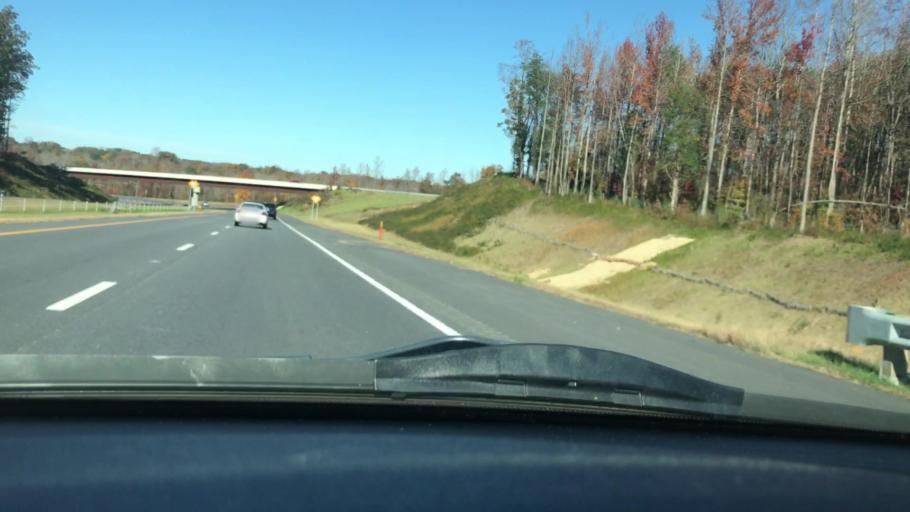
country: US
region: North Carolina
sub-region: Guilford County
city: Summerfield
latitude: 36.2232
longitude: -79.9139
